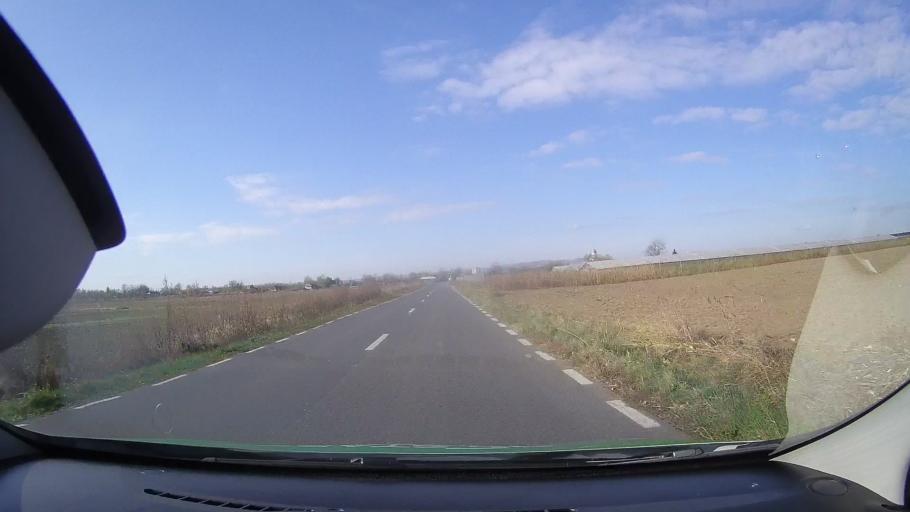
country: RO
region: Tulcea
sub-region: Comuna Valea Nucarilor
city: Iazurile
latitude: 45.0225
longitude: 28.9532
